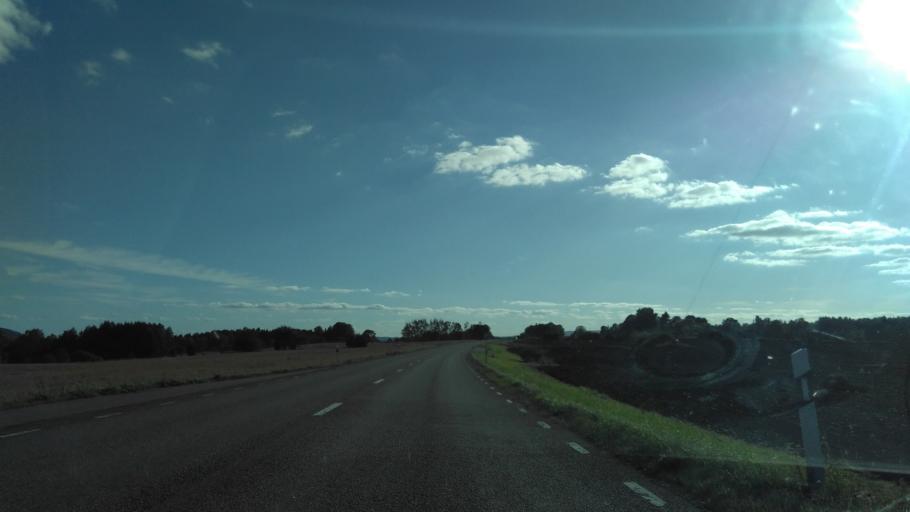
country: SE
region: Vaestra Goetaland
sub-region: Skovde Kommun
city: Skultorp
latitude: 58.2766
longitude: 13.7542
